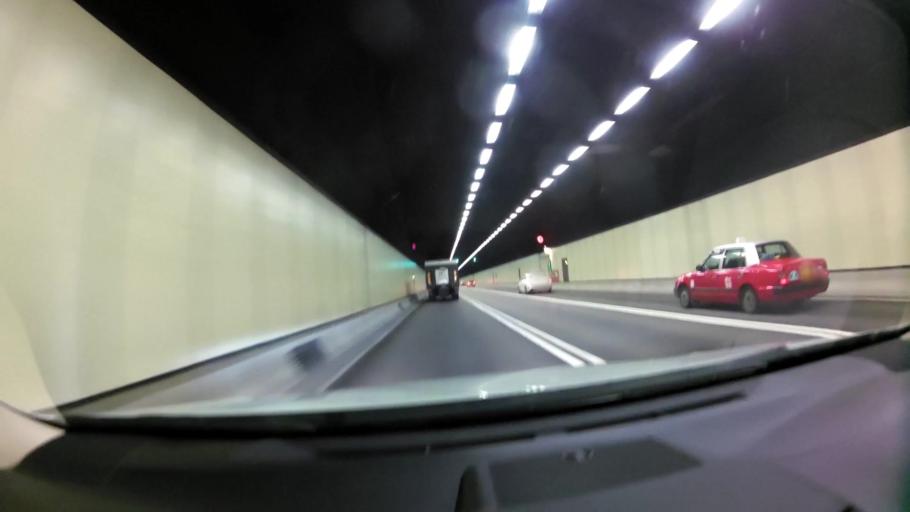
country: HK
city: Hong Kong
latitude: 22.2953
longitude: 114.1500
